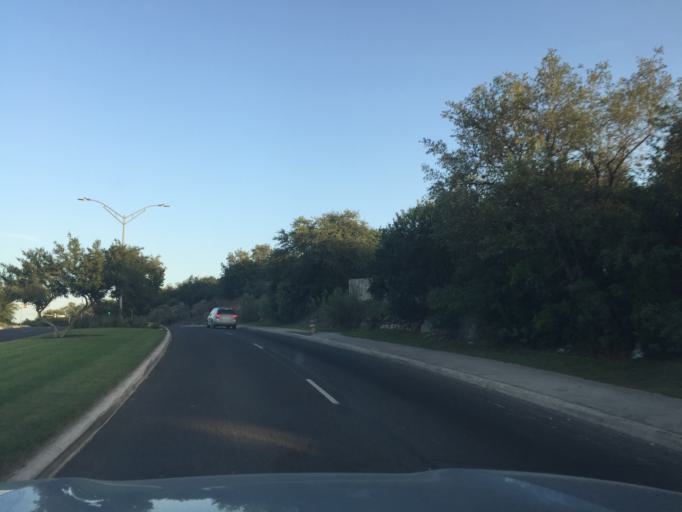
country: US
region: Texas
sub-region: Bexar County
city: Hollywood Park
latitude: 29.6407
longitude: -98.4805
